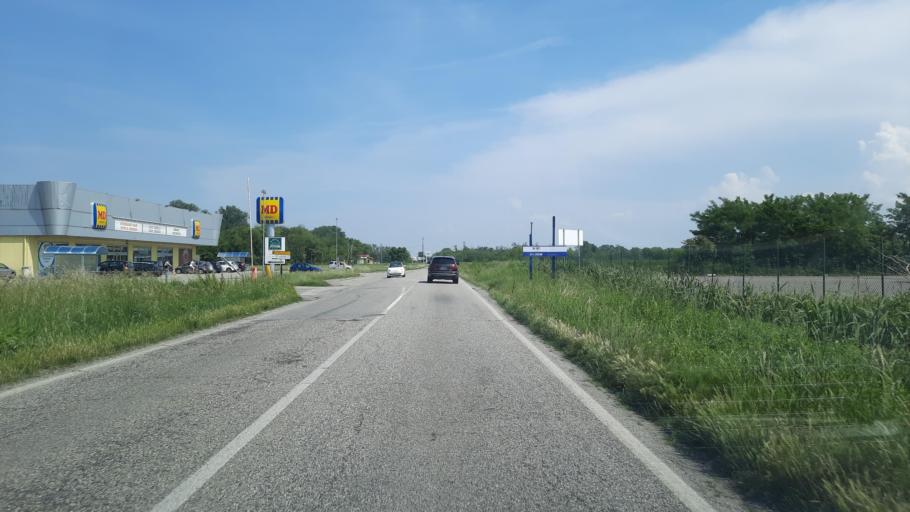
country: IT
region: Lombardy
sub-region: Provincia di Pavia
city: Villanova d'Ardenghi
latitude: 45.1639
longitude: 9.0219
